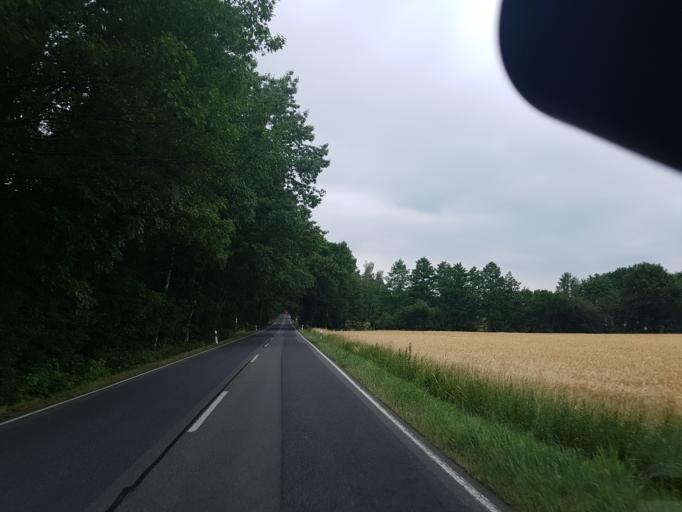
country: DE
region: Brandenburg
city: Lebusa
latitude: 51.8108
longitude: 13.4209
